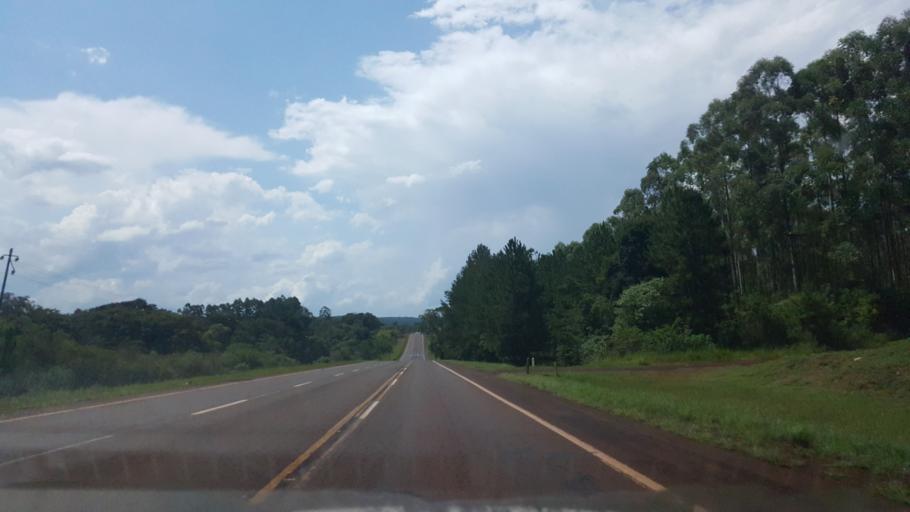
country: AR
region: Misiones
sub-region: Departamento de Eldorado
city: Eldorado
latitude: -26.3754
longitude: -54.6255
